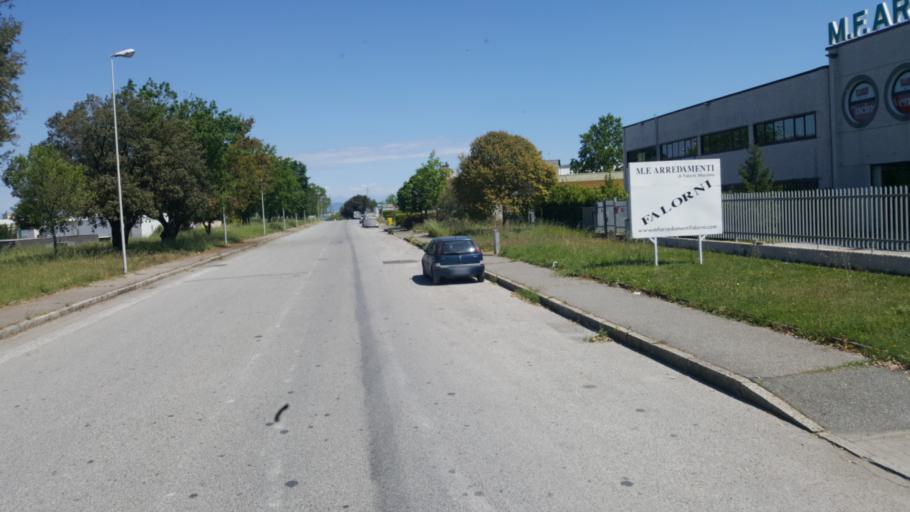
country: IT
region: Tuscany
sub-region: Provincia di Livorno
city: Livorno
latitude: 43.5720
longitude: 10.3431
